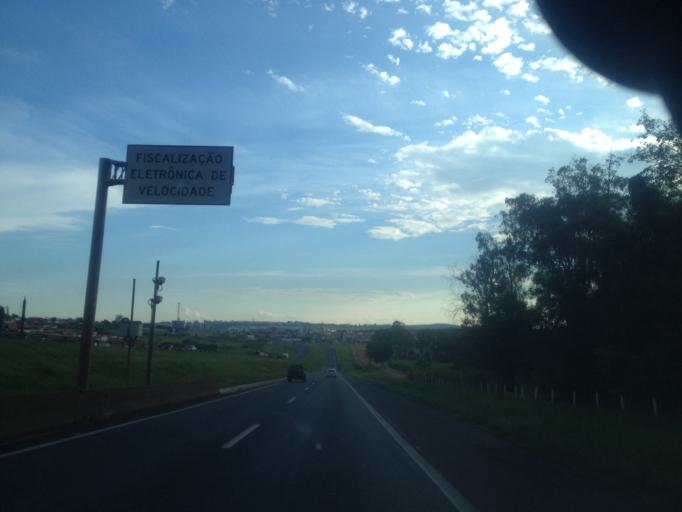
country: BR
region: Sao Paulo
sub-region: Araras
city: Araras
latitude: -22.3368
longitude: -47.3904
